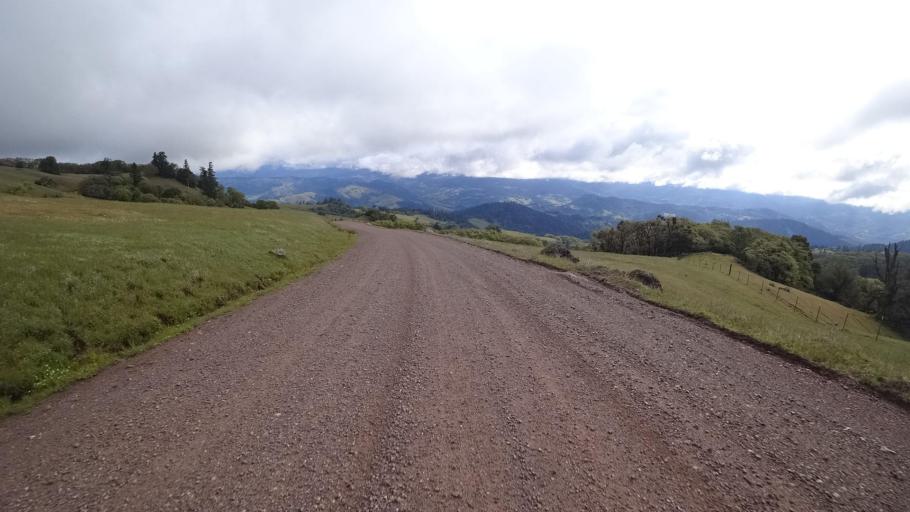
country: US
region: California
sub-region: Humboldt County
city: Redway
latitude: 40.1952
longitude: -123.7023
